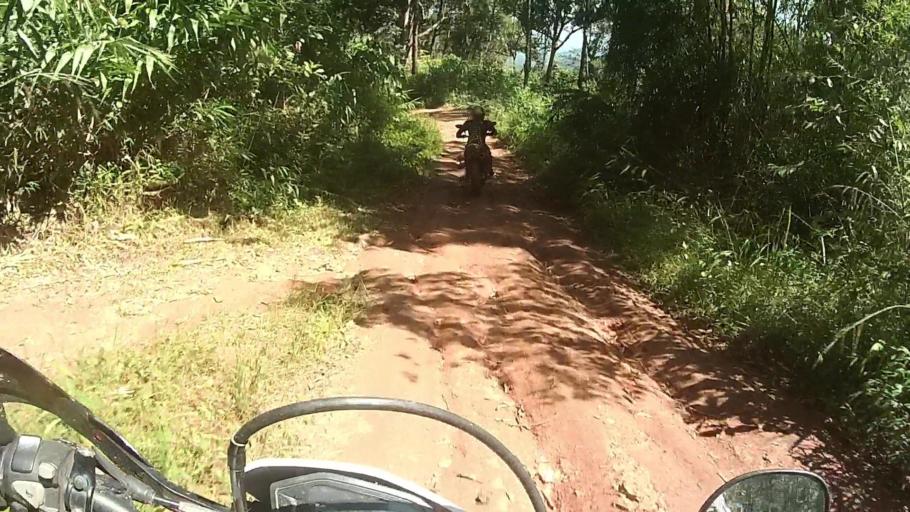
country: TH
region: Chiang Mai
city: Phrao
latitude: 19.4860
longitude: 99.3108
